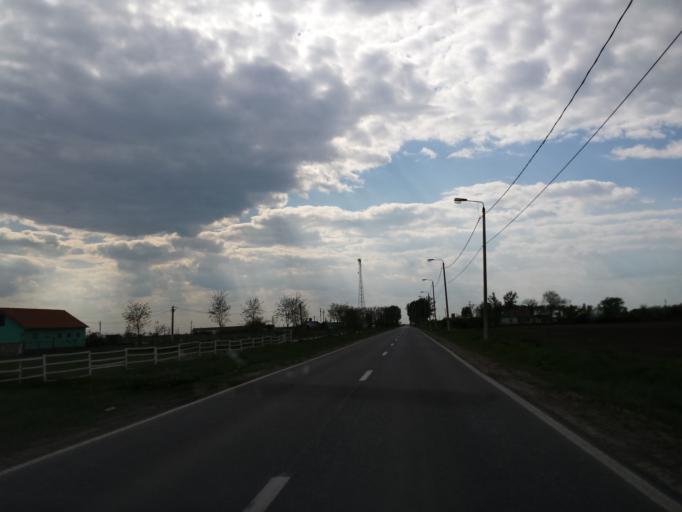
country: RO
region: Timis
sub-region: Comuna Cenad
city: Cenad
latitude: 46.1290
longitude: 20.5605
